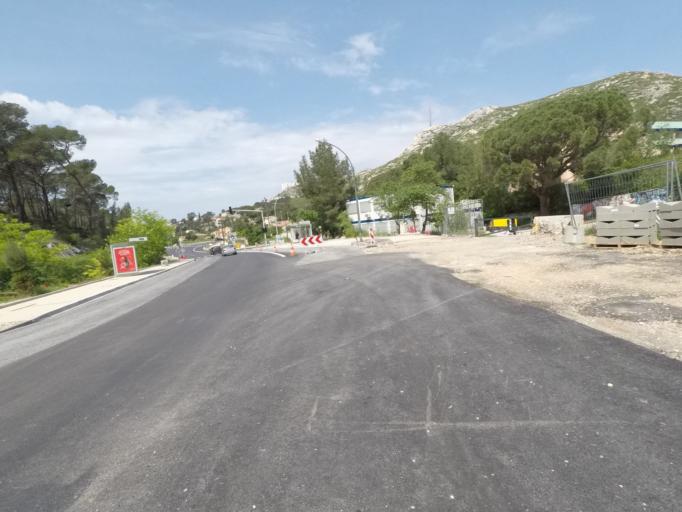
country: FR
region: Provence-Alpes-Cote d'Azur
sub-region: Departement des Bouches-du-Rhone
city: Marseille 09
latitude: 43.2462
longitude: 5.4369
